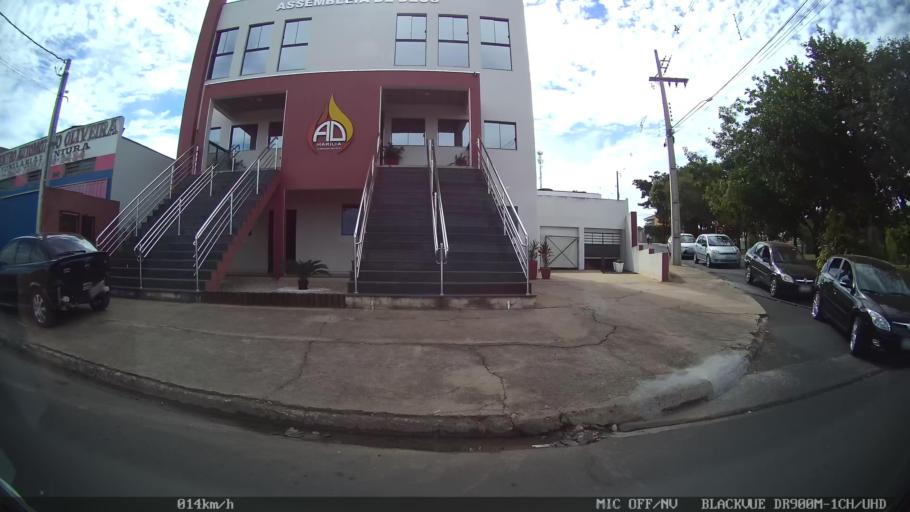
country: BR
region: Sao Paulo
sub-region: Catanduva
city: Catanduva
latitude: -21.1418
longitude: -48.9519
